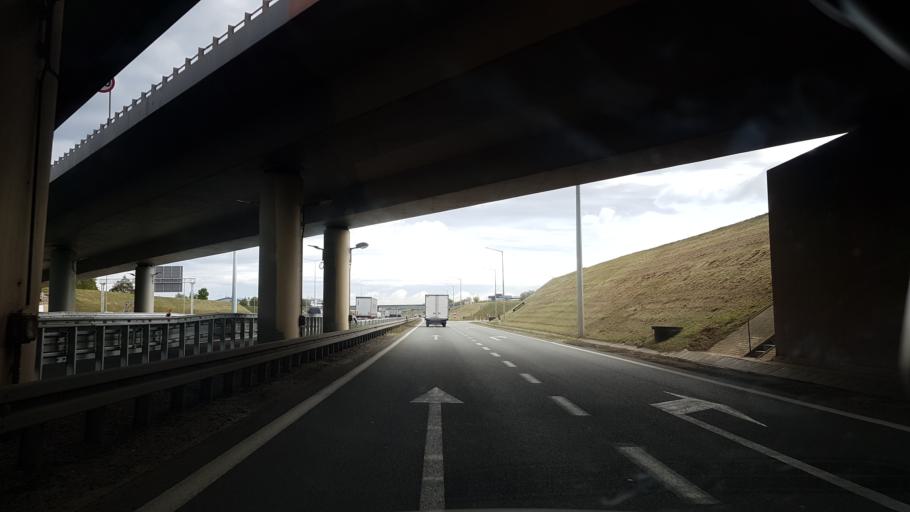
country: PL
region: Greater Poland Voivodeship
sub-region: Powiat poznanski
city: Komorniki
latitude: 52.3501
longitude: 16.8366
